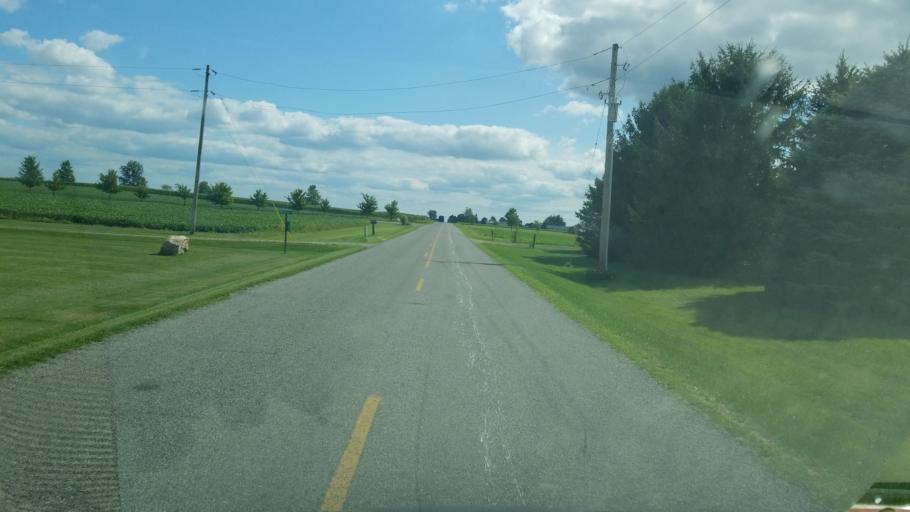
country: US
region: Ohio
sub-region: Logan County
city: Lakeview
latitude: 40.5495
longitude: -83.9749
